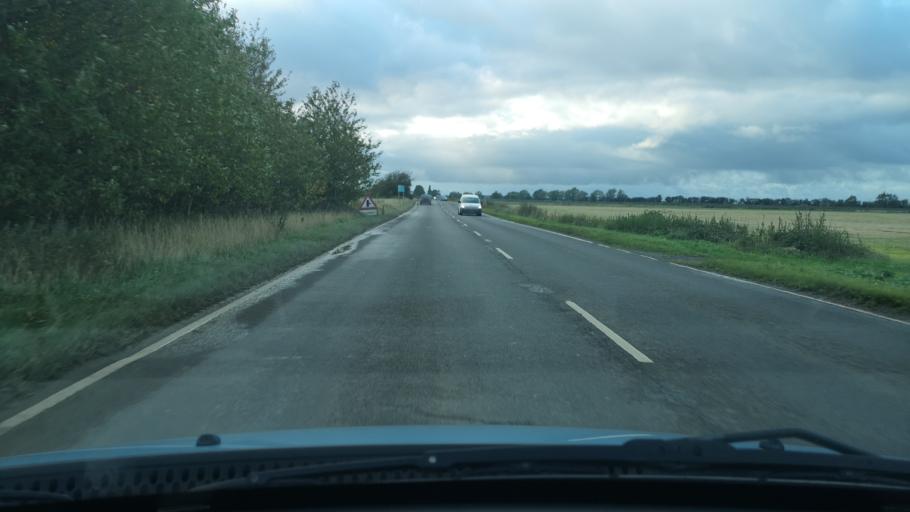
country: GB
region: England
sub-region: North Lincolnshire
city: Gunness
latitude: 53.5776
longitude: -0.7632
